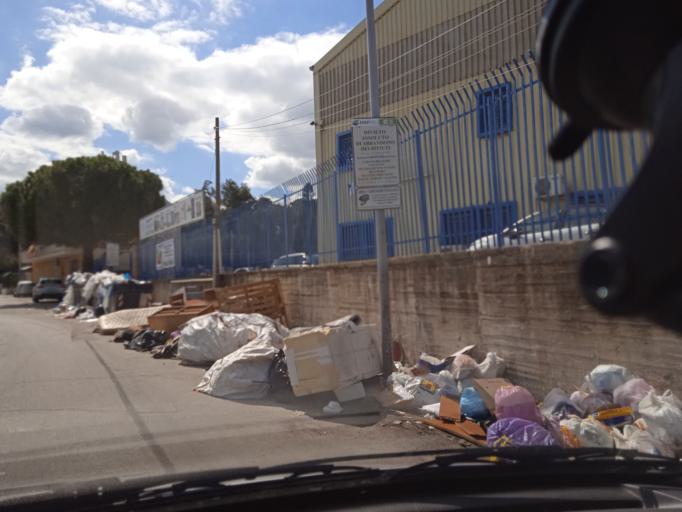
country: IT
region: Sicily
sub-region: Palermo
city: Ciaculli
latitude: 38.0870
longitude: 13.4222
